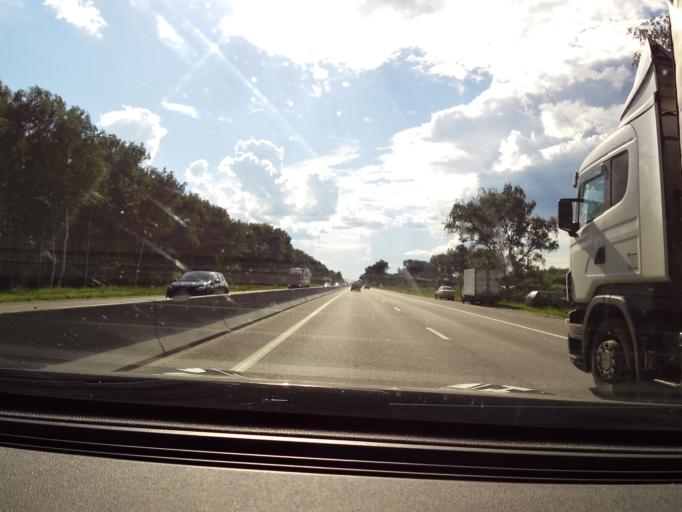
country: RU
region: Nizjnij Novgorod
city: Babino
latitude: 56.3052
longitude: 43.6424
